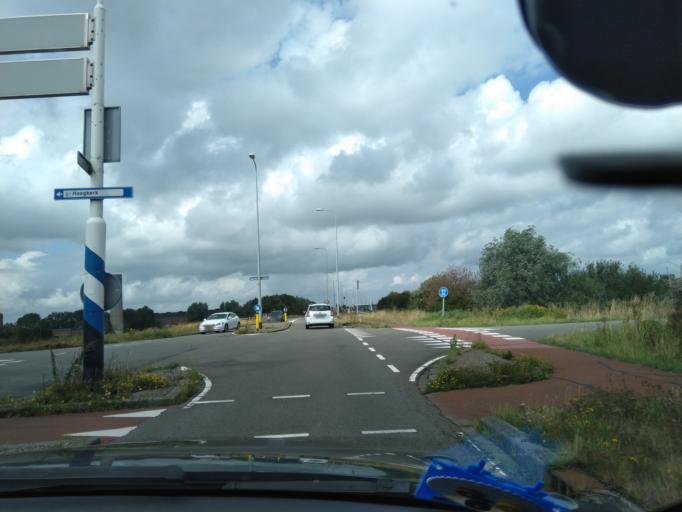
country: NL
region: Groningen
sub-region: Gemeente Groningen
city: Groningen
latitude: 53.2102
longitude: 6.5140
